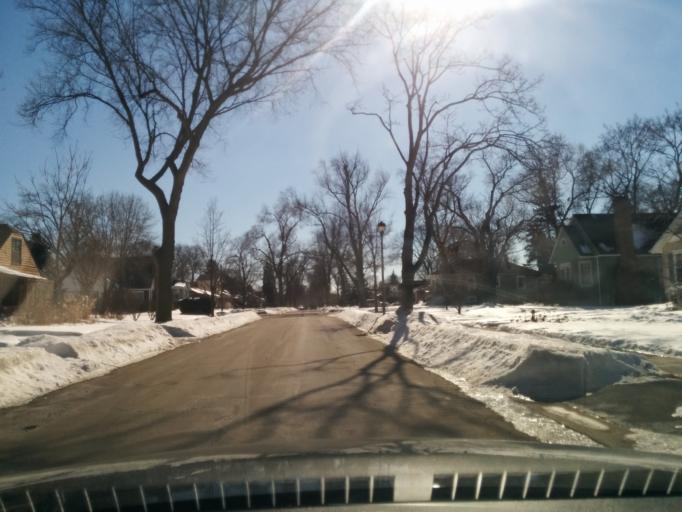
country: US
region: Illinois
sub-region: DuPage County
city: Villa Park
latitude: 41.8944
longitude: -87.9679
